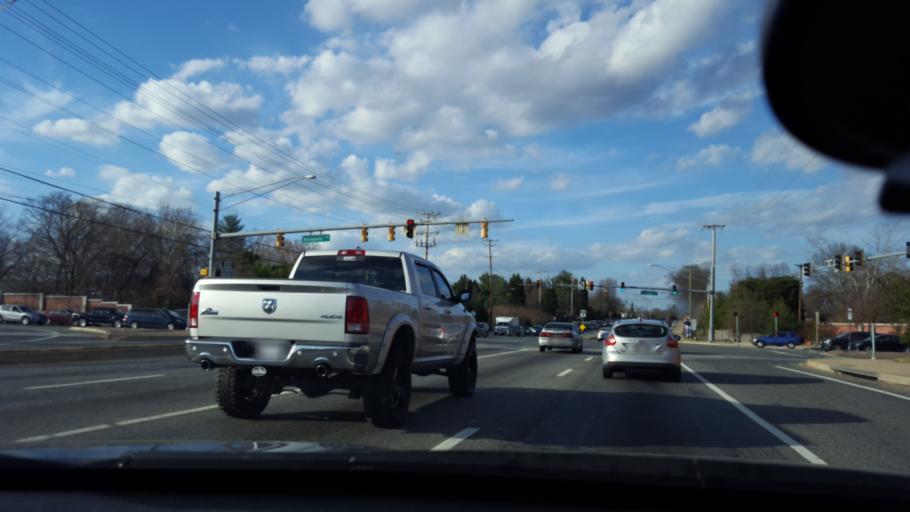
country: US
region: Maryland
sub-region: Prince George's County
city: Bowie
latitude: 38.9734
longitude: -76.7558
